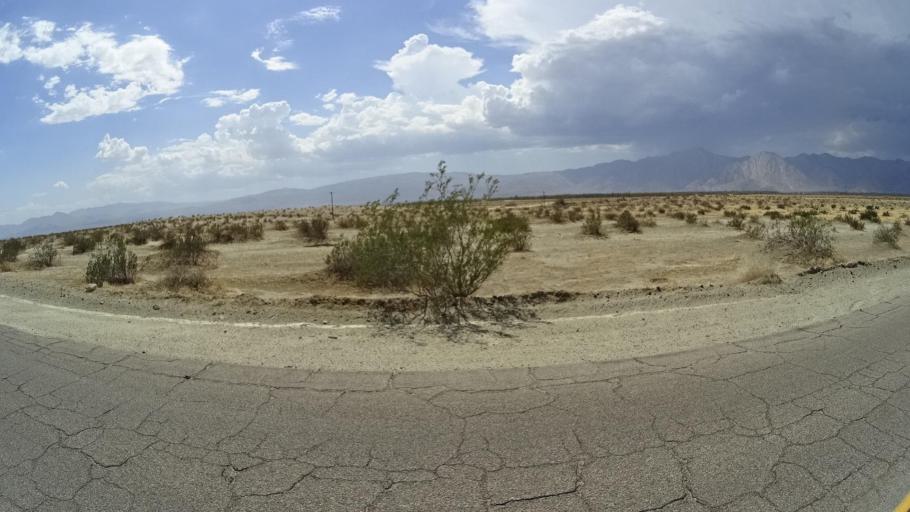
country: US
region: California
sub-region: San Diego County
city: Borrego Springs
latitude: 33.2974
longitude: -116.3101
